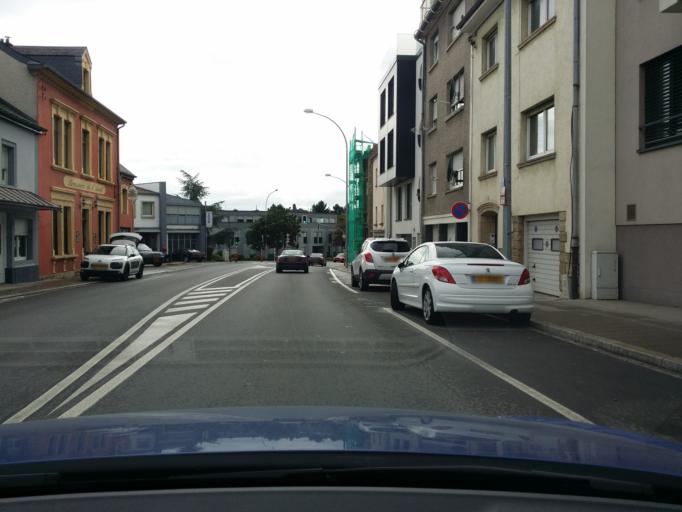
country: LU
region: Luxembourg
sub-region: Canton de Luxembourg
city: Strassen
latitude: 49.6036
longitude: 6.0923
